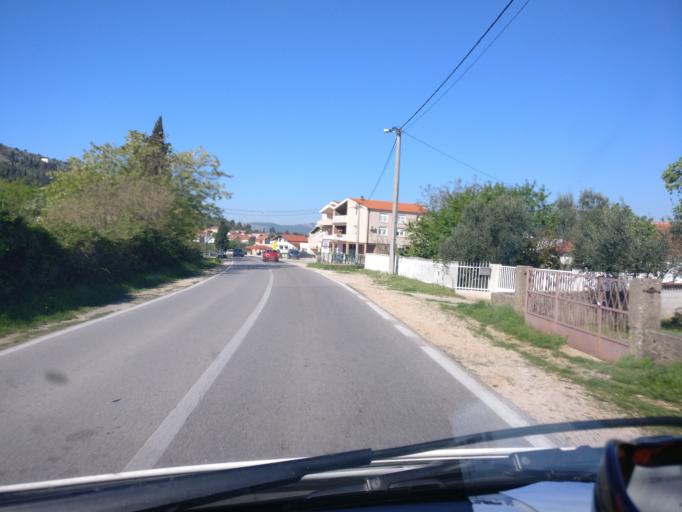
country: BA
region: Federation of Bosnia and Herzegovina
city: Tasovcici
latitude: 43.1199
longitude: 17.7414
